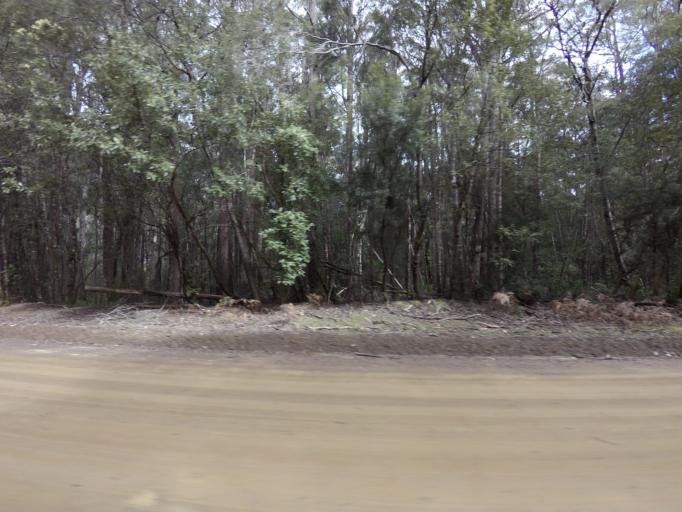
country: AU
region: Tasmania
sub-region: Huon Valley
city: Geeveston
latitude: -43.4115
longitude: 146.8733
